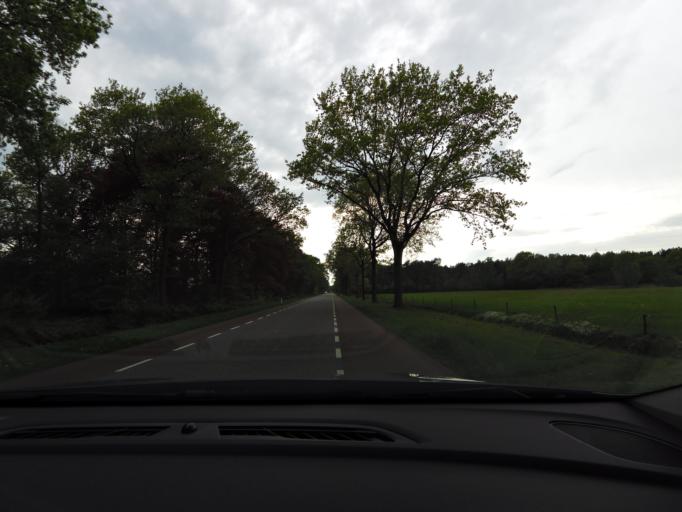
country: NL
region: North Brabant
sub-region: Gemeente Loon op Zand
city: Loon op Zand
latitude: 51.6111
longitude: 5.0934
